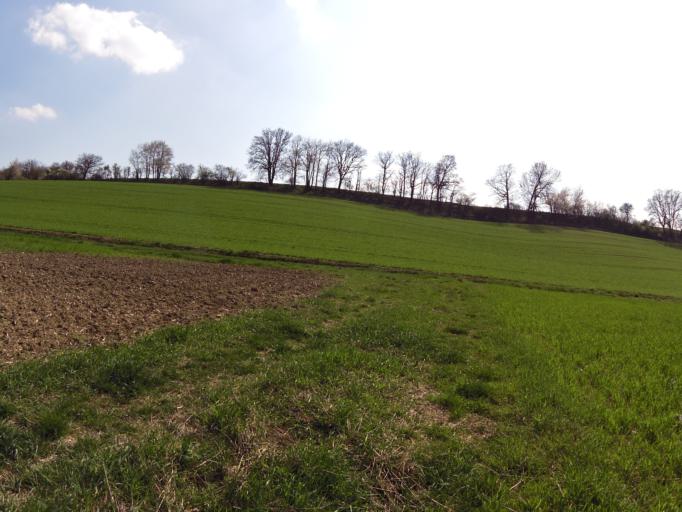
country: DE
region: Bavaria
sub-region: Regierungsbezirk Unterfranken
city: Rottendorf
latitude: 49.7806
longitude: 10.0358
